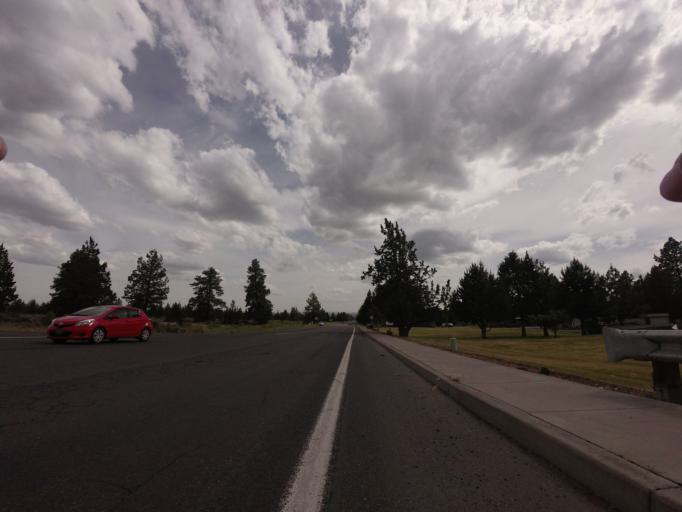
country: US
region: Oregon
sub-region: Deschutes County
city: Bend
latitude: 44.0349
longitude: -121.2638
